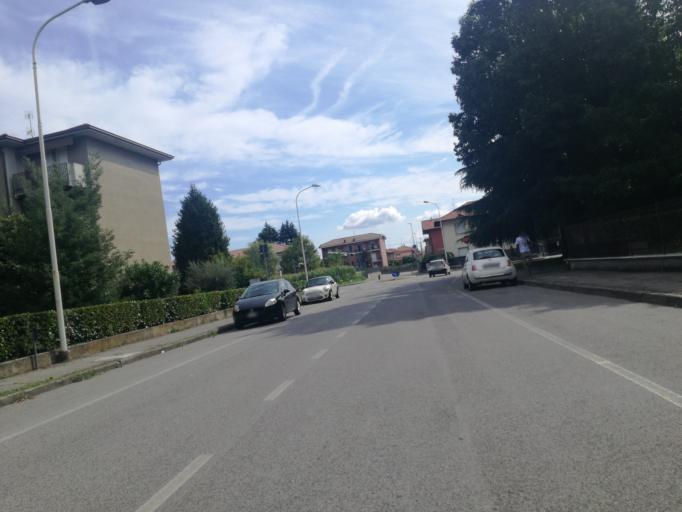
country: IT
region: Lombardy
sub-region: Provincia di Bergamo
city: Calusco d'Adda
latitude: 45.6899
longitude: 9.4650
